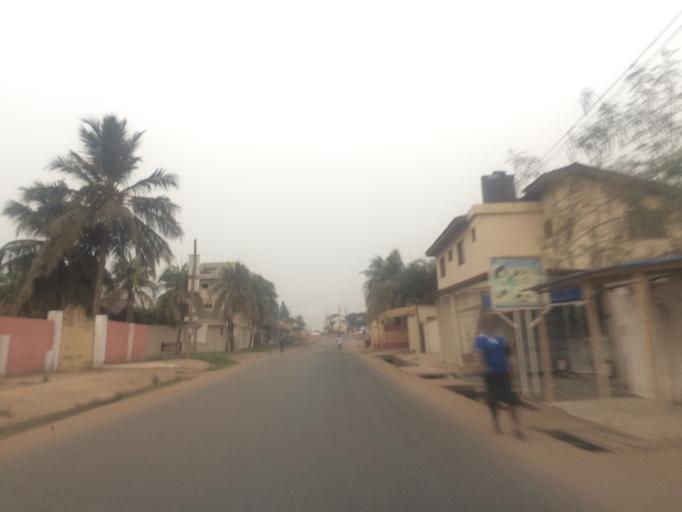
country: GH
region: Greater Accra
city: Teshi Old Town
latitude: 5.5981
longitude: -0.1008
